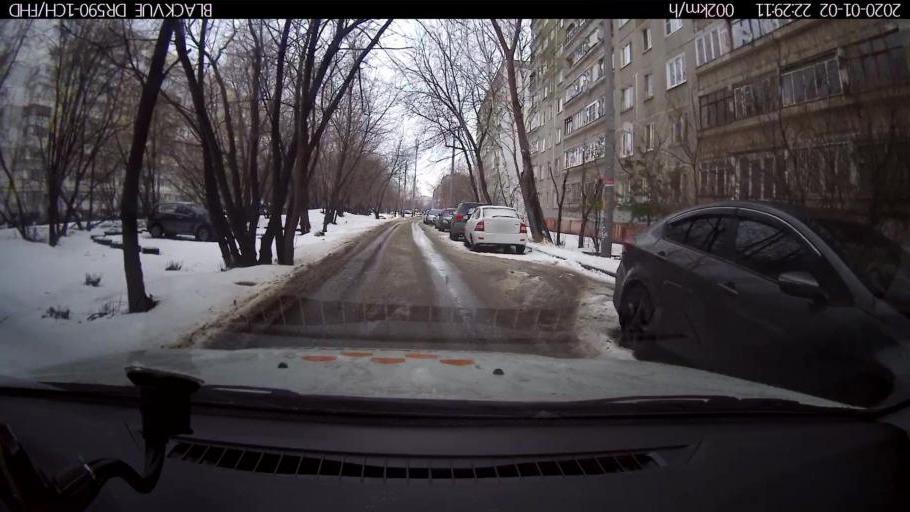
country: RU
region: Nizjnij Novgorod
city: Nizhniy Novgorod
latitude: 56.3266
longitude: 43.9294
